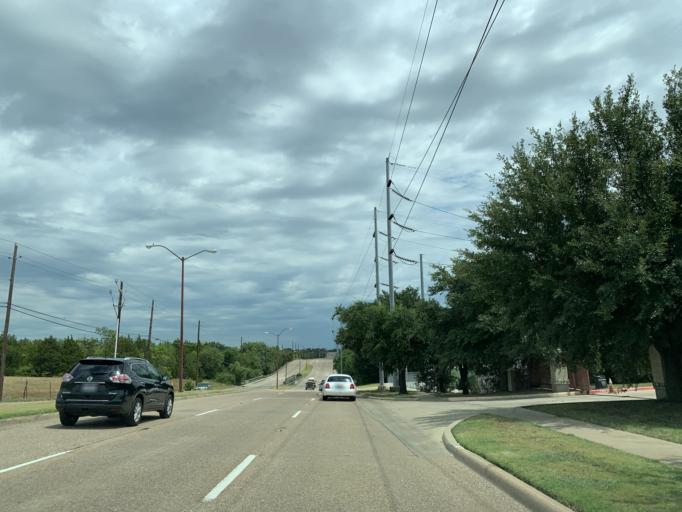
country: US
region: Texas
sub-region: Dallas County
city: DeSoto
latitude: 32.6622
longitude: -96.8162
